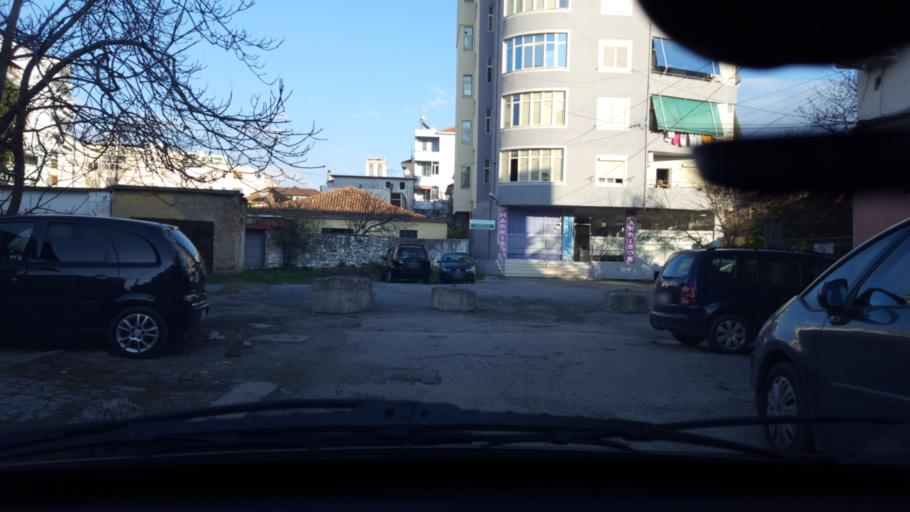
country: AL
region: Elbasan
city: Elbasan
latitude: 41.1159
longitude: 20.0857
